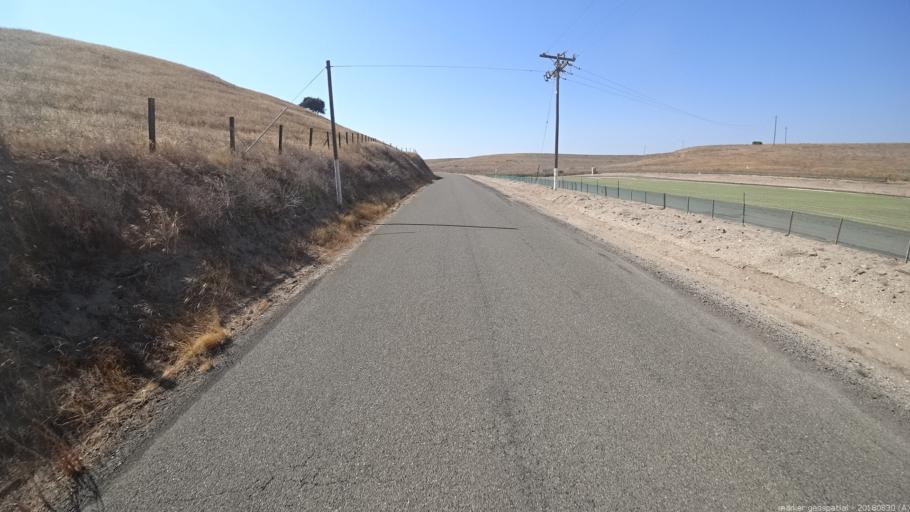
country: US
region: California
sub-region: Monterey County
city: King City
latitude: 36.1084
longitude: -121.0529
